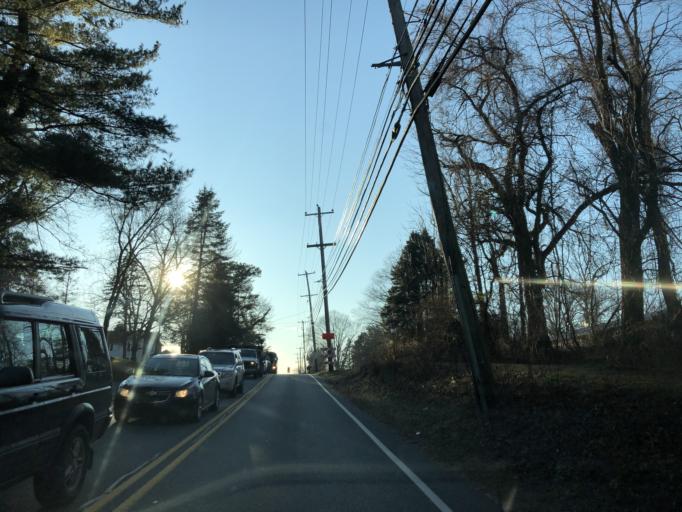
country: US
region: Pennsylvania
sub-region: Delaware County
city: Chester Heights
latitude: 39.8711
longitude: -75.5039
